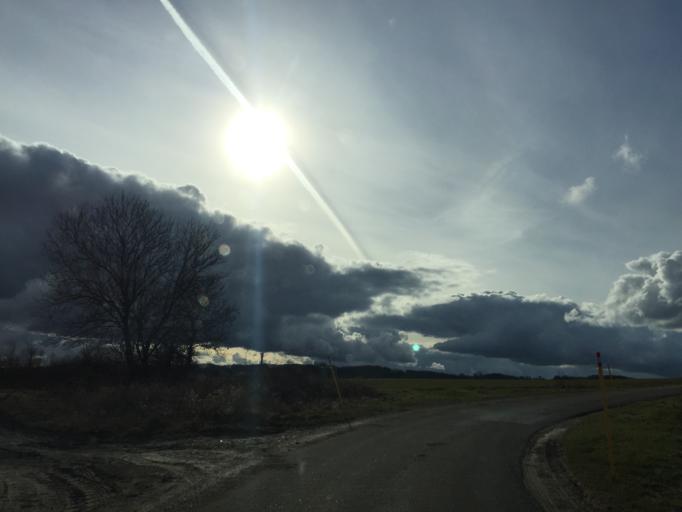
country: DK
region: Central Jutland
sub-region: Favrskov Kommune
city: Hammel
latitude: 56.2009
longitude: 9.8036
